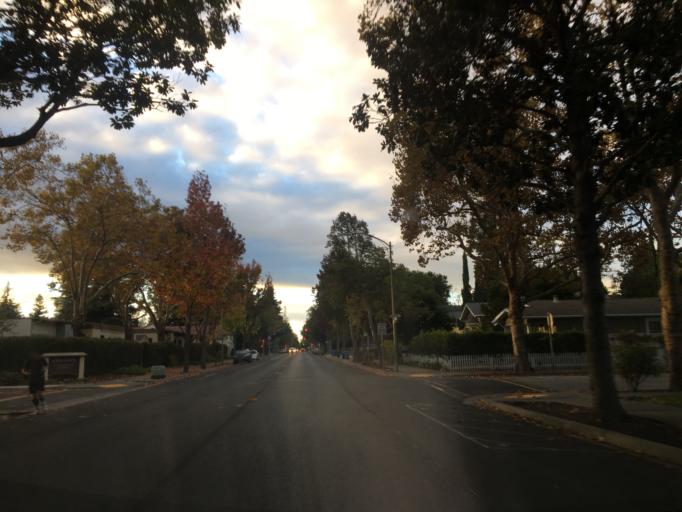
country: US
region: California
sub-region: Santa Clara County
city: Palo Alto
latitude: 37.4458
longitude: -122.1490
